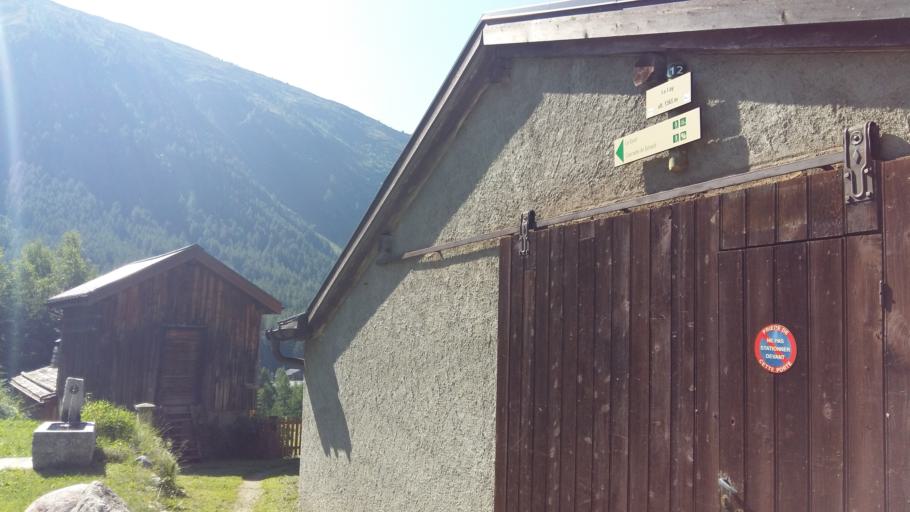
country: FR
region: Rhone-Alpes
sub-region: Departement de la Haute-Savoie
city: Chamonix-Mont-Blanc
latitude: 46.0218
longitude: 6.9169
